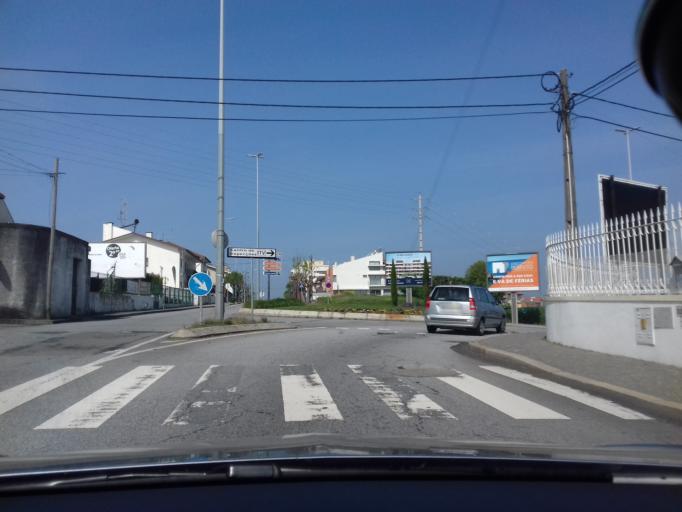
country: PT
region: Aveiro
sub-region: Espinho
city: Silvalde
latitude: 41.0084
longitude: -8.6243
